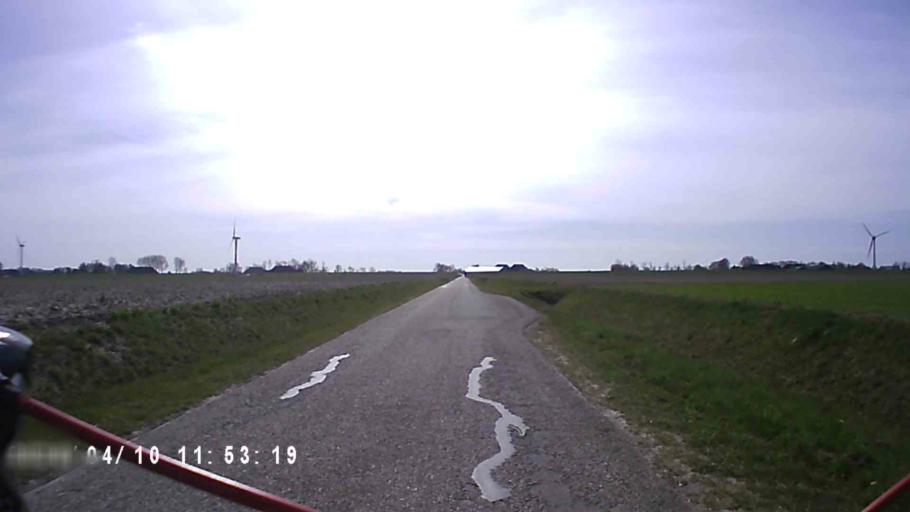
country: NL
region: Groningen
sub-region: Gemeente De Marne
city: Ulrum
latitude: 53.3916
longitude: 6.3326
